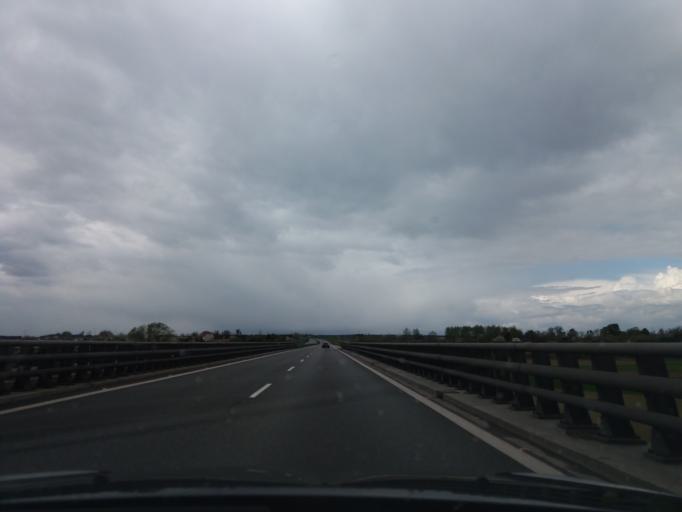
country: PL
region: Opole Voivodeship
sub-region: Powiat krapkowicki
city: Krapkowice
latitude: 50.5165
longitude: 17.9532
